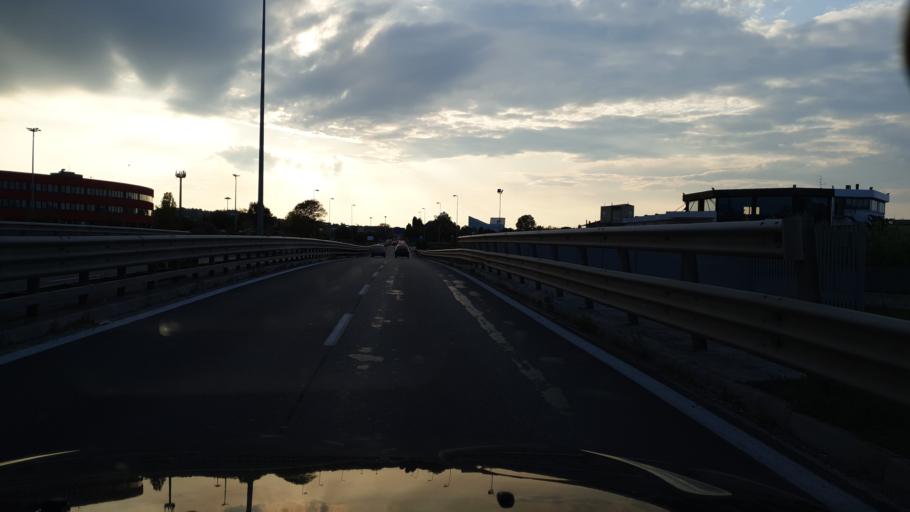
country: IT
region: Emilia-Romagna
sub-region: Provincia di Rimini
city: Rimini
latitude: 44.0416
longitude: 12.5818
